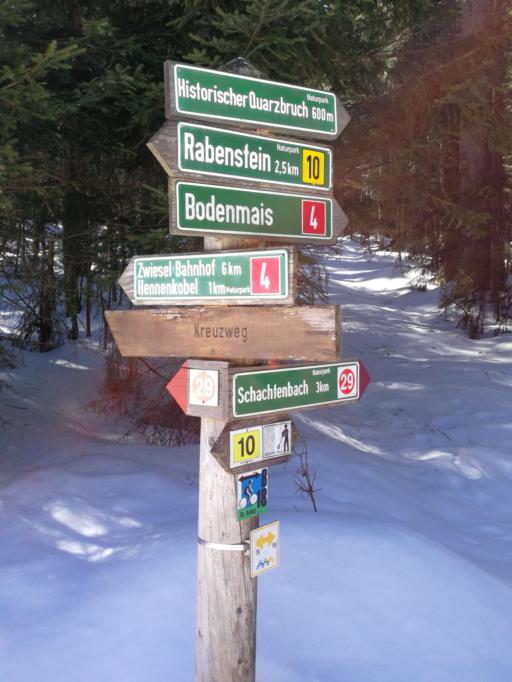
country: DE
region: Bavaria
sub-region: Lower Bavaria
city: Langdorf
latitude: 49.0498
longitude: 13.1761
